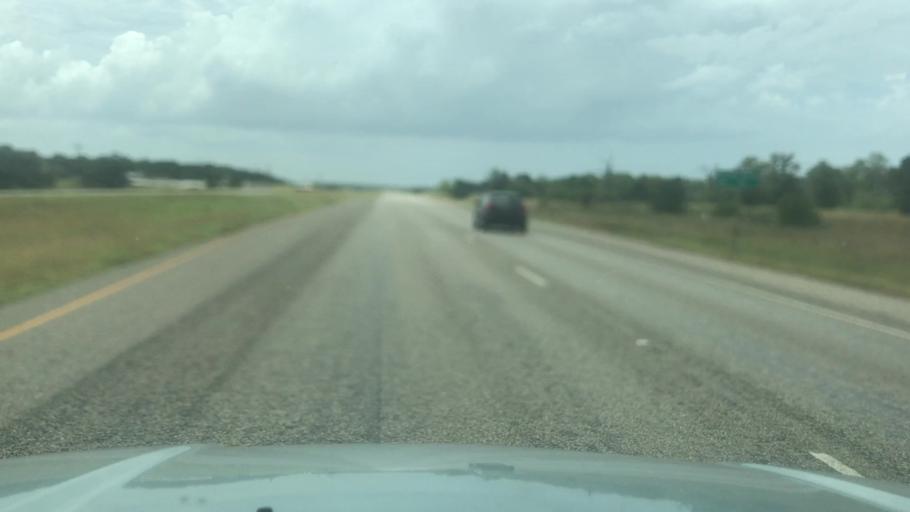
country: US
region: Texas
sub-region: Colorado County
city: Columbus
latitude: 29.7846
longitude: -96.6467
